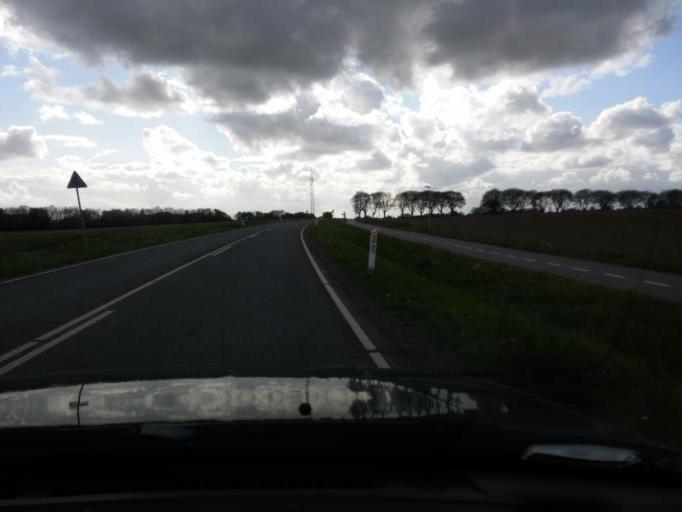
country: DK
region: South Denmark
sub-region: Faaborg-Midtfyn Kommune
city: Ringe
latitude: 55.2453
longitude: 10.5223
